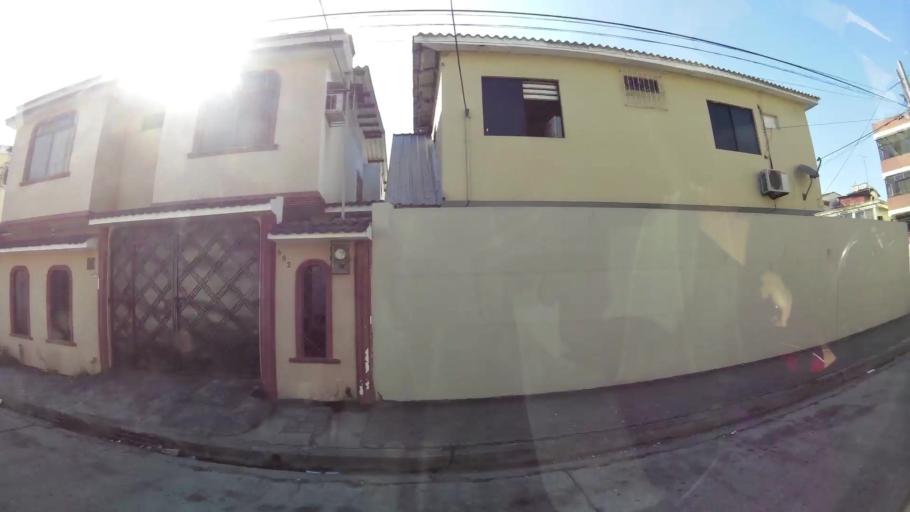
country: EC
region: Guayas
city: Guayaquil
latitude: -2.1731
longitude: -79.8973
